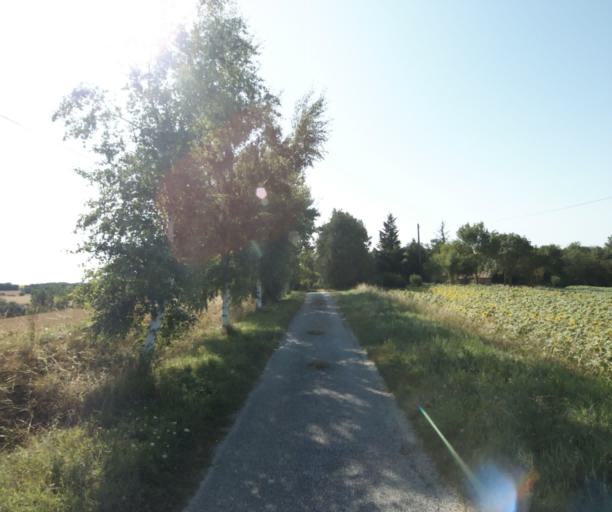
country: FR
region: Midi-Pyrenees
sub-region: Departement de la Haute-Garonne
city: Avignonet-Lauragais
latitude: 43.4232
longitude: 1.8104
